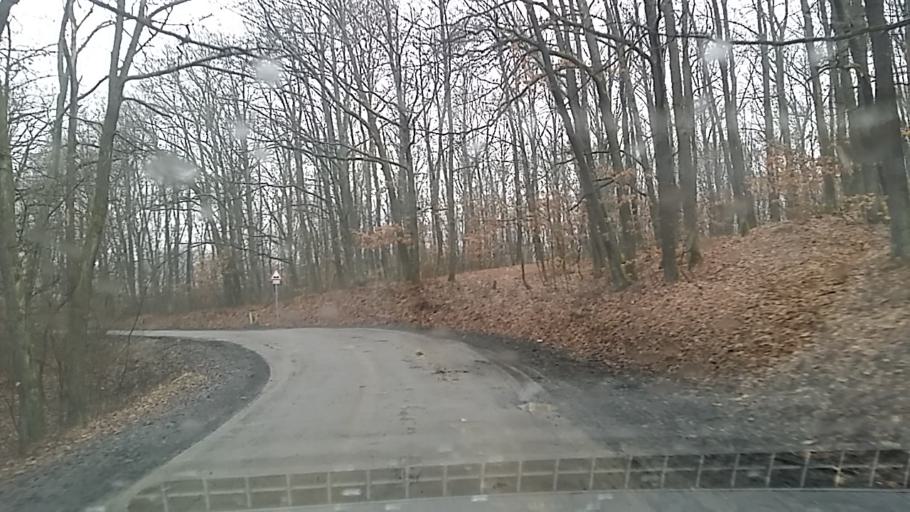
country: HU
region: Borsod-Abauj-Zemplen
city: Rudabanya
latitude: 48.4173
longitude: 20.5752
